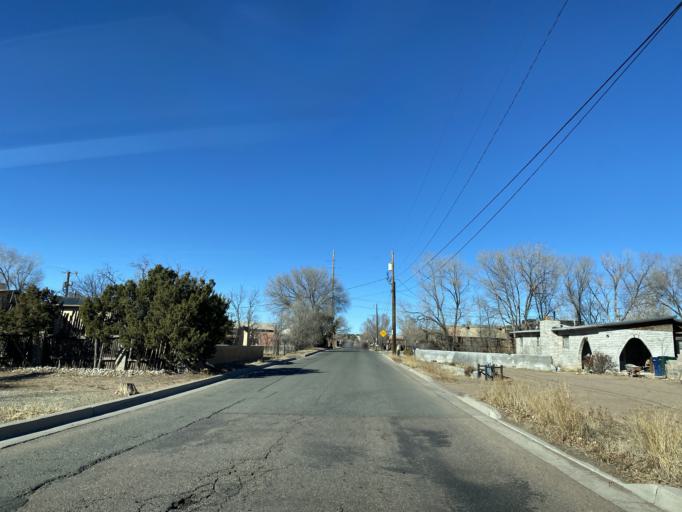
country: US
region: New Mexico
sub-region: Santa Fe County
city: Agua Fria
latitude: 35.6621
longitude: -105.9887
